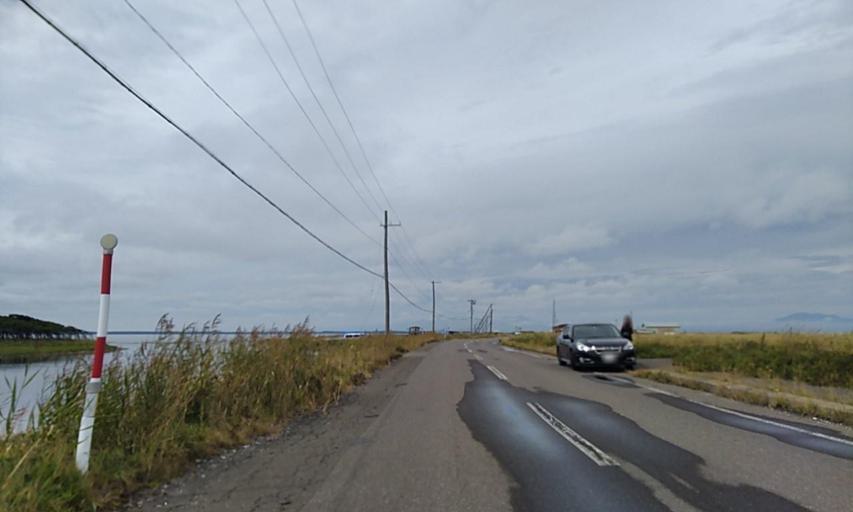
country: JP
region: Hokkaido
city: Shibetsu
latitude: 43.6095
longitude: 145.2725
